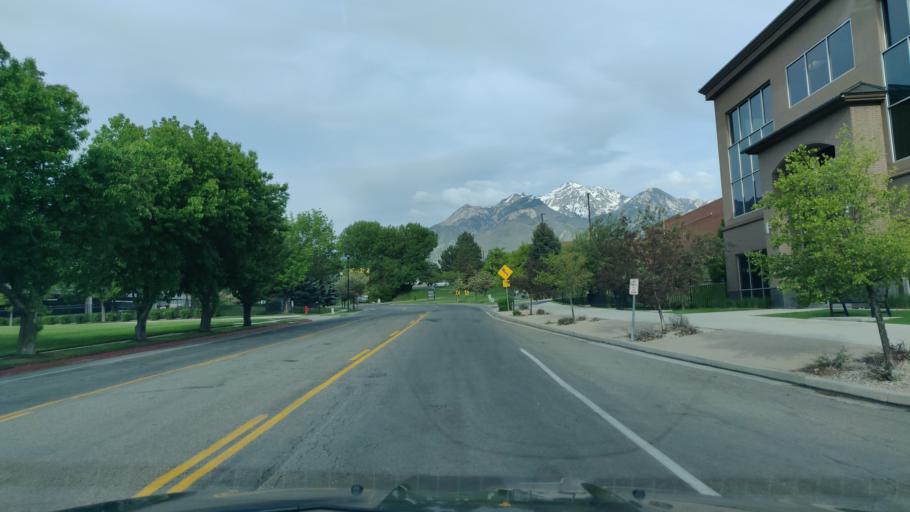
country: US
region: Utah
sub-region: Salt Lake County
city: Little Cottonwood Creek Valley
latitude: 40.6096
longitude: -111.8566
